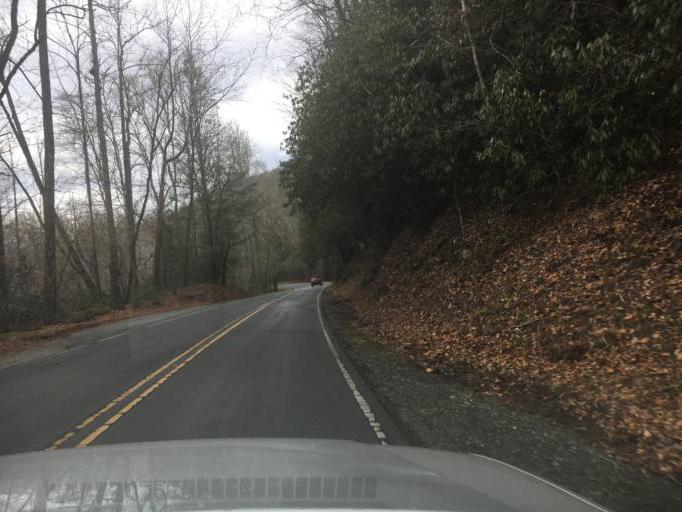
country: US
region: North Carolina
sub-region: Transylvania County
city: Brevard
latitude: 35.2772
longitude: -82.7127
